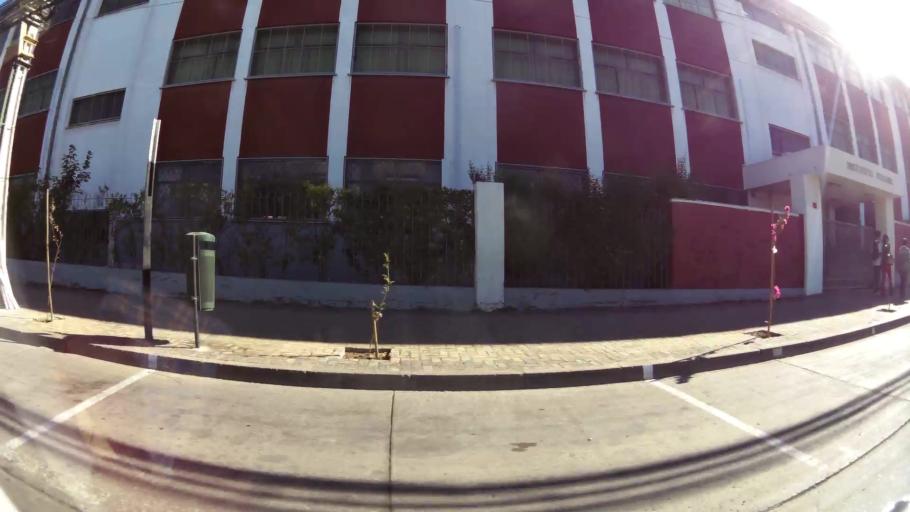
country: CL
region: O'Higgins
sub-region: Provincia de Cachapoal
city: Rancagua
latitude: -34.1747
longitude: -70.7426
